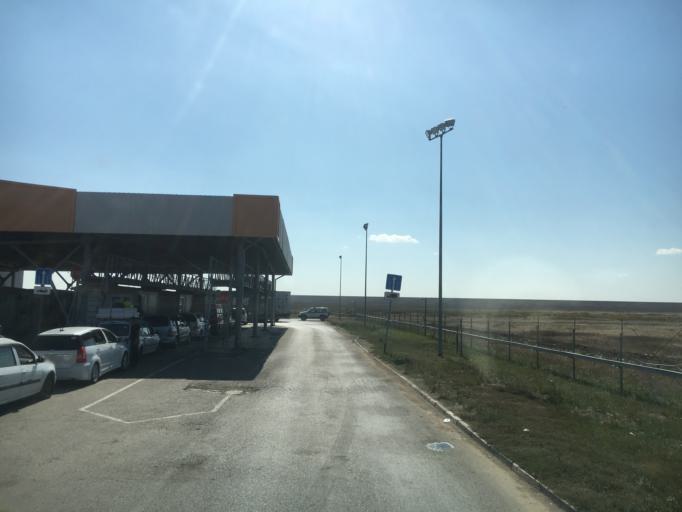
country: KZ
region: Batys Qazaqstan
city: Peremetnoe
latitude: 51.6780
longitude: 50.9993
